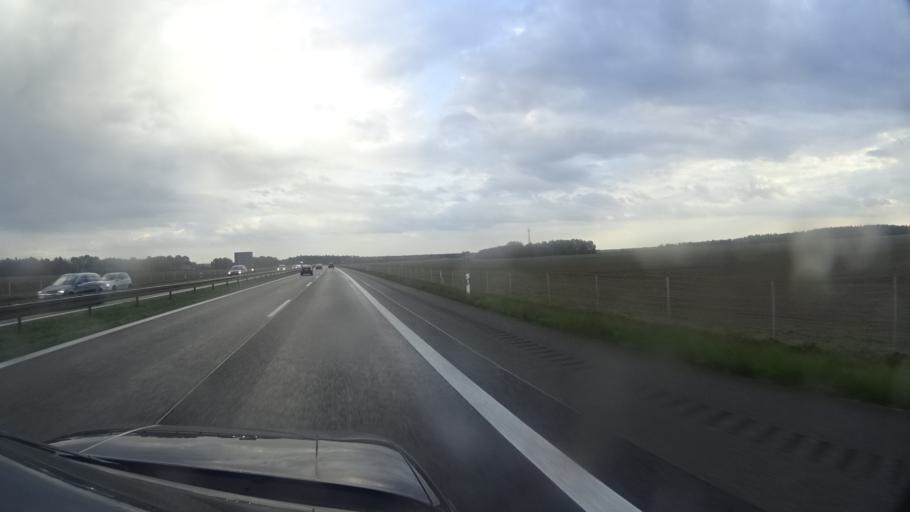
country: DE
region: Brandenburg
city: Wittstock
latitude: 53.0631
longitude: 12.5316
